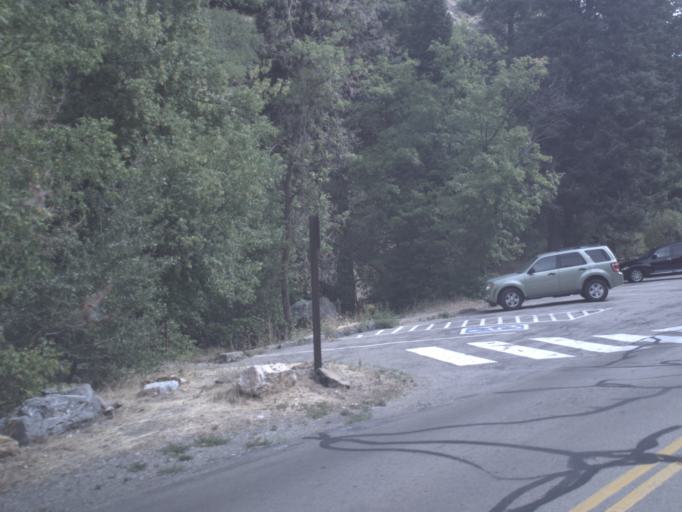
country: US
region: Utah
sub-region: Utah County
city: Cedar Hills
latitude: 40.4439
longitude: -111.7058
